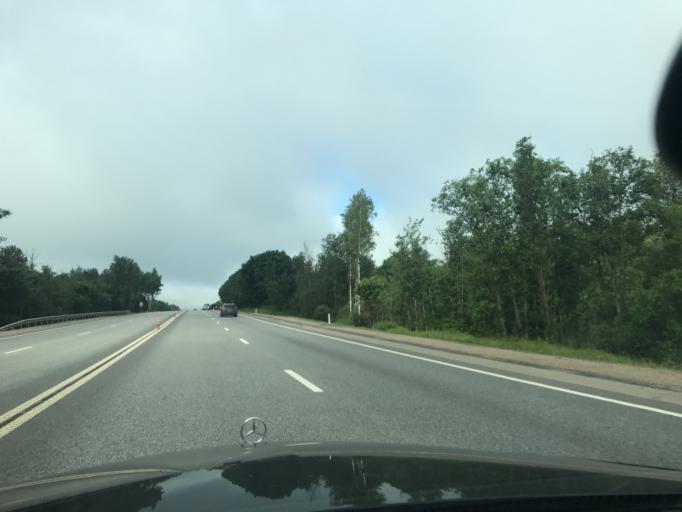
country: RU
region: Smolensk
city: Vyaz'ma
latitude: 55.2860
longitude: 34.4471
